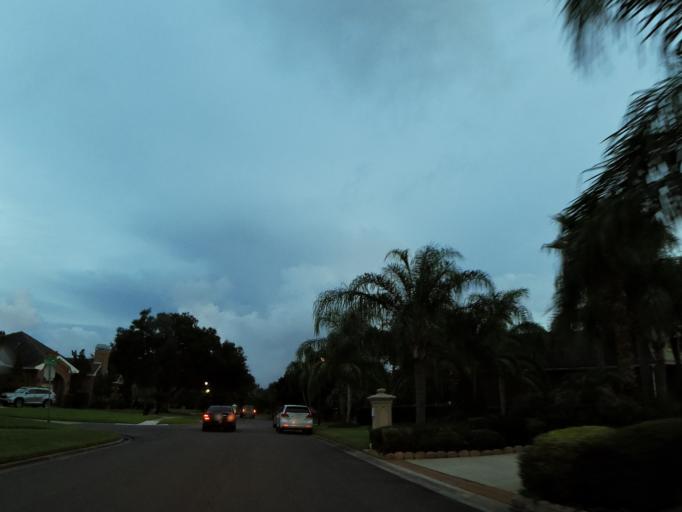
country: US
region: Florida
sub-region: Duval County
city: Jacksonville
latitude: 30.3841
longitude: -81.6217
